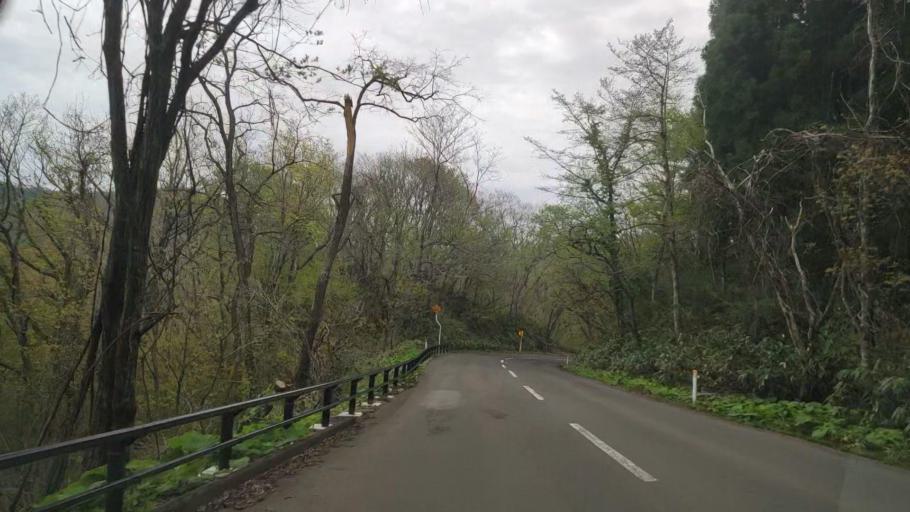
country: JP
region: Akita
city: Hanawa
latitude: 40.3740
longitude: 140.7900
